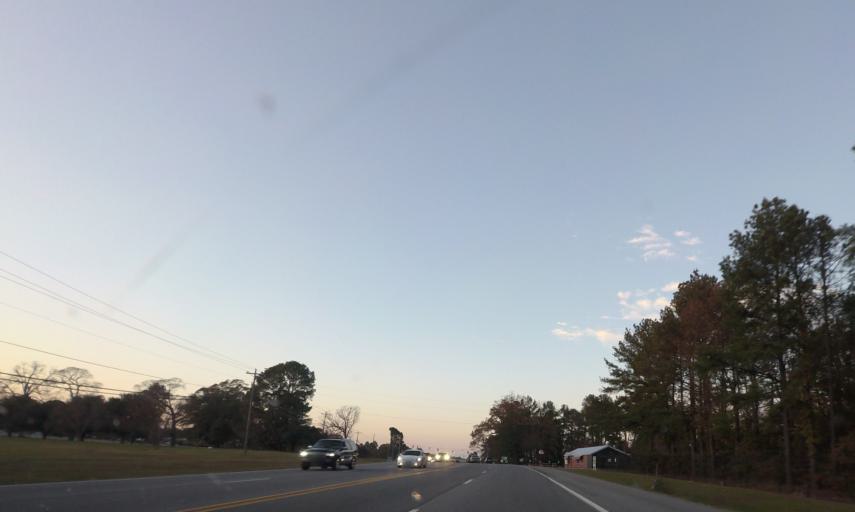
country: US
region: Georgia
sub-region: Houston County
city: Robins Air Force Base
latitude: 32.5881
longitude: -83.5878
